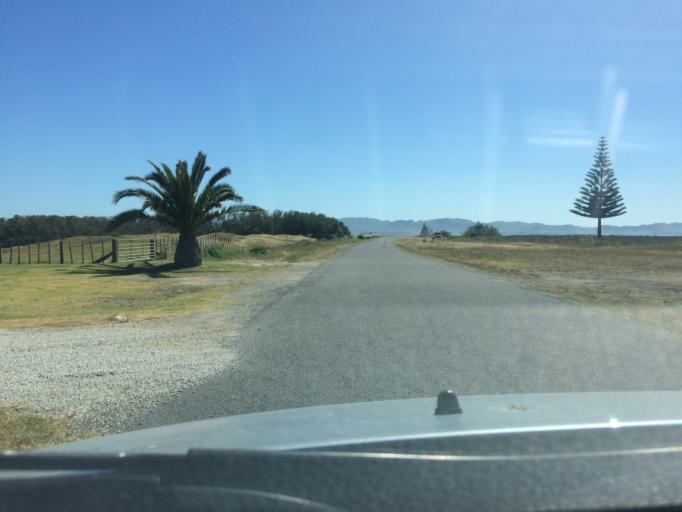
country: NZ
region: Gisborne
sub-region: Gisborne District
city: Gisborne
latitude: -38.6935
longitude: 177.9554
